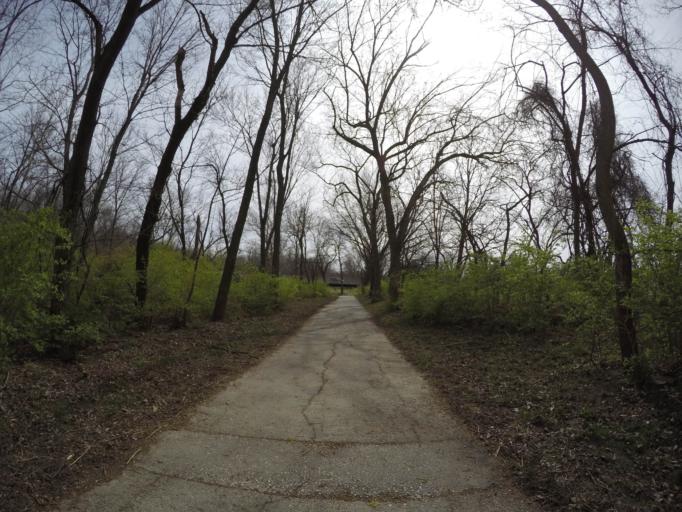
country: US
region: Kansas
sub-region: Johnson County
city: Leawood
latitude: 38.9139
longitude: -94.6327
